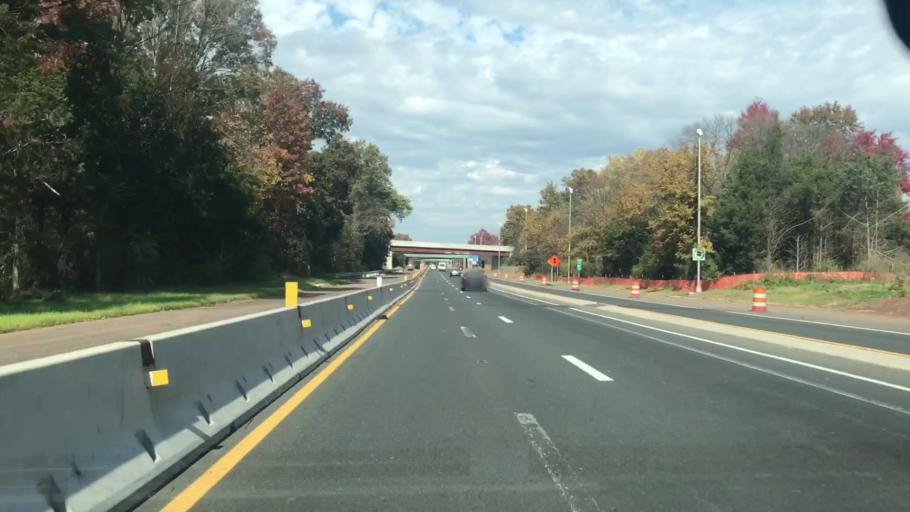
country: US
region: New Jersey
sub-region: Somerset County
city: Bridgewater
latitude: 40.6395
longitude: -74.6445
